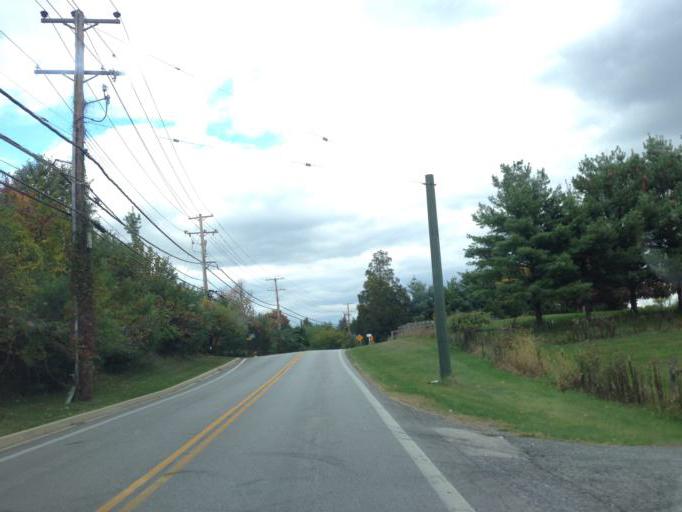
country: US
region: Maryland
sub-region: Howard County
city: Ellicott City
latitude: 39.3037
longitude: -76.8066
